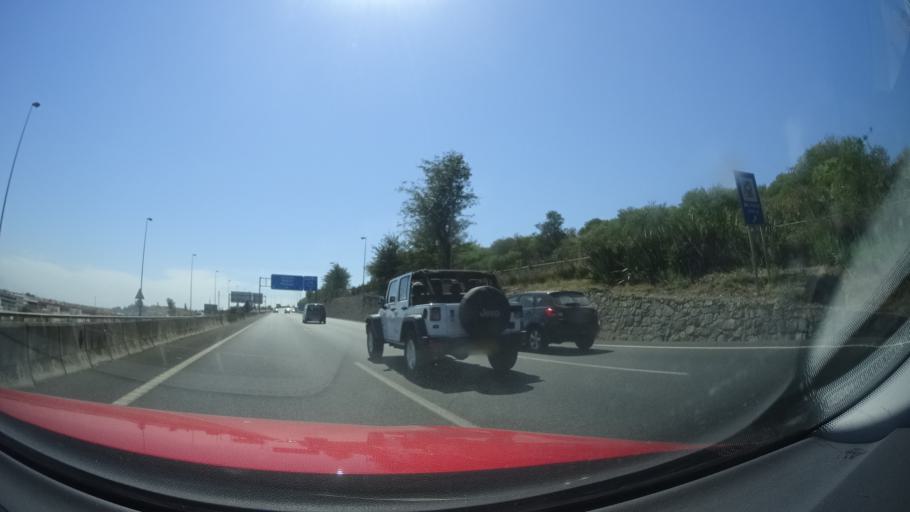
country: ES
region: Andalusia
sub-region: Provincia de Sevilla
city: Camas
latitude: 37.3870
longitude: -6.0342
